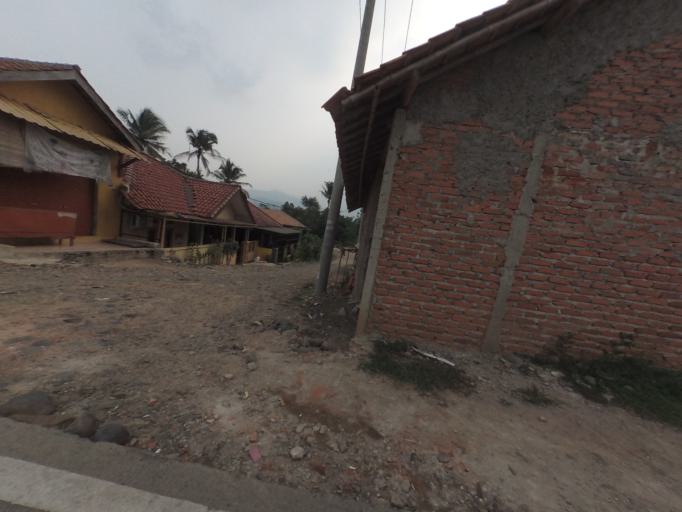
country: ID
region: West Java
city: Sidoger Lebak
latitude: -6.5634
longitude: 106.5837
